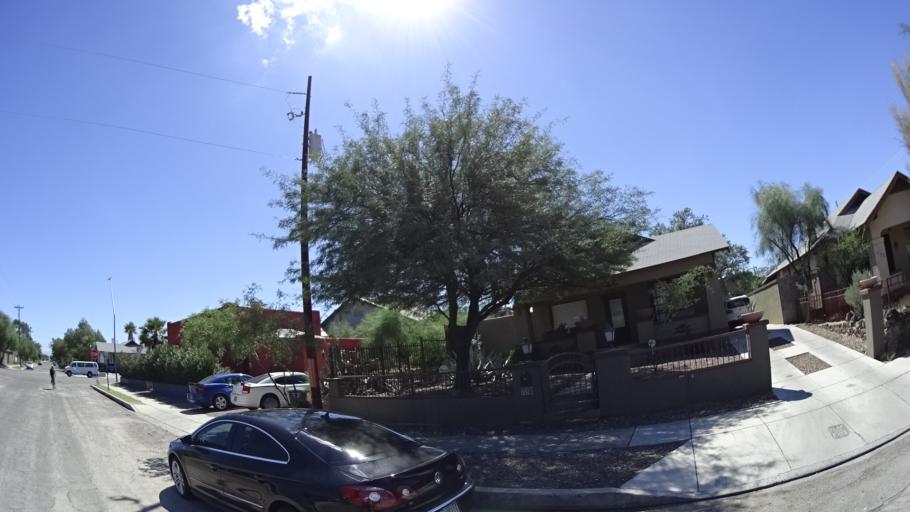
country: US
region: Arizona
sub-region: Pima County
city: Tucson
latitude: 32.2385
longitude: -110.9601
